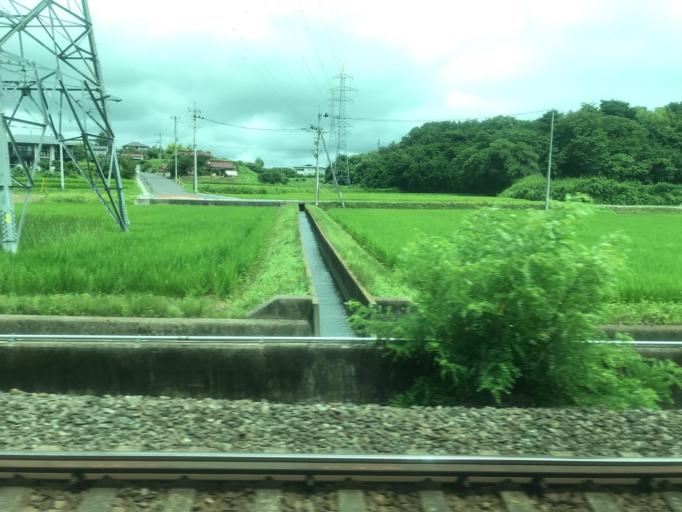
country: JP
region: Fukushima
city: Koriyama
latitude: 37.4505
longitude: 140.3850
